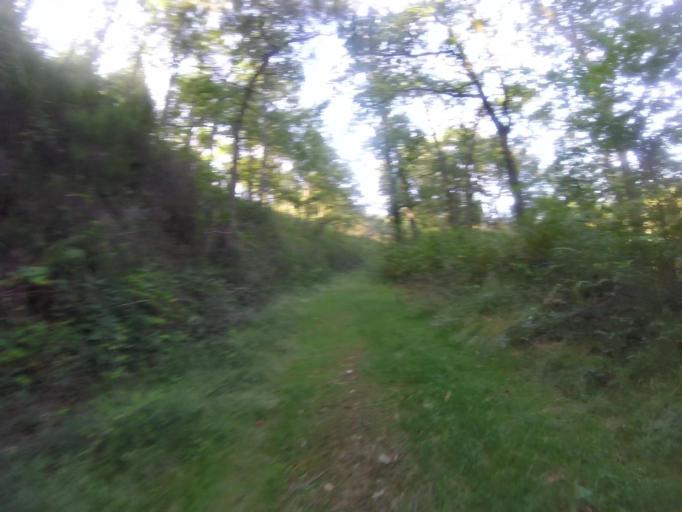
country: ES
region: Navarre
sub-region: Provincia de Navarra
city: Arano
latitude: 43.2318
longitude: -1.9051
